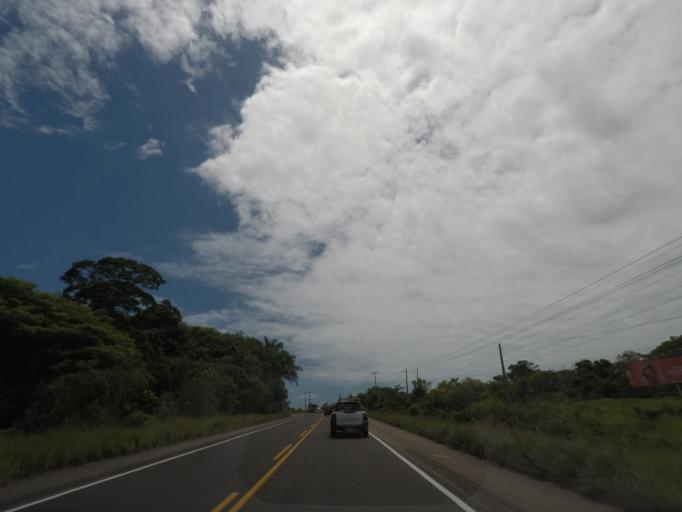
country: BR
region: Bahia
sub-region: Itaparica
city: Itaparica
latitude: -12.9736
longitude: -38.6355
